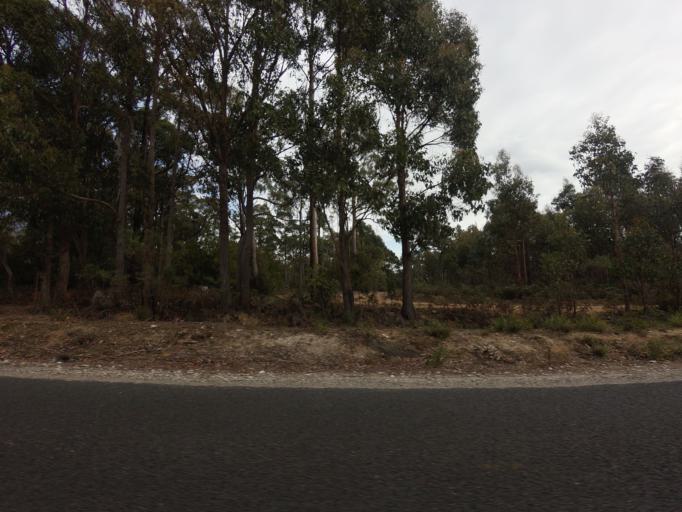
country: AU
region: Tasmania
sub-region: Meander Valley
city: Deloraine
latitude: -41.6138
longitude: 146.6888
